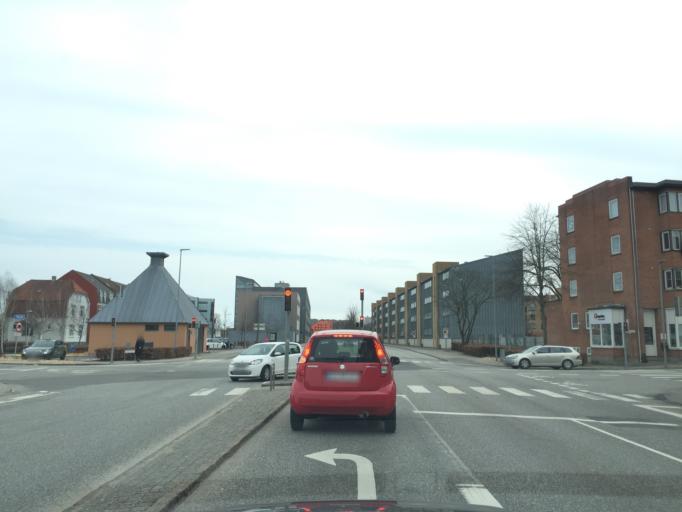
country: DK
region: South Denmark
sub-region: Kolding Kommune
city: Kolding
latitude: 55.4862
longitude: 9.4769
